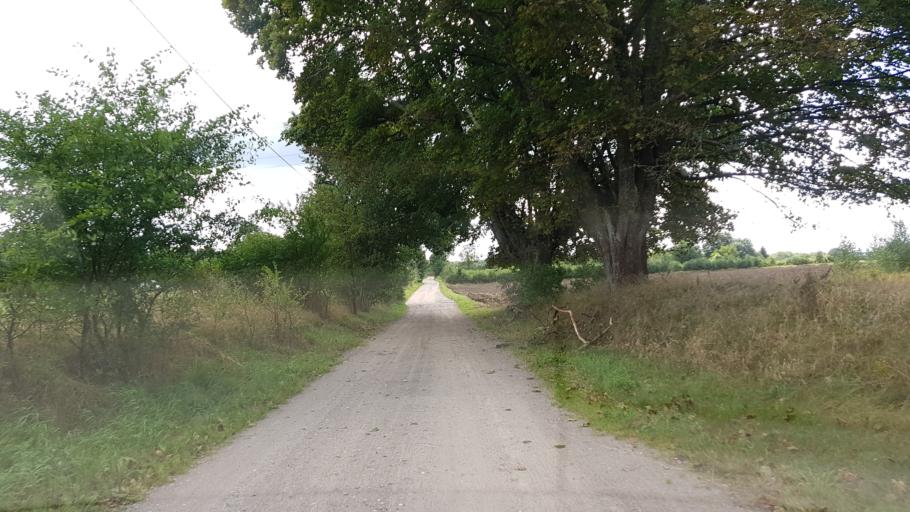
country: PL
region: West Pomeranian Voivodeship
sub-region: Powiat bialogardzki
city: Tychowo
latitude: 53.9966
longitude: 16.3051
